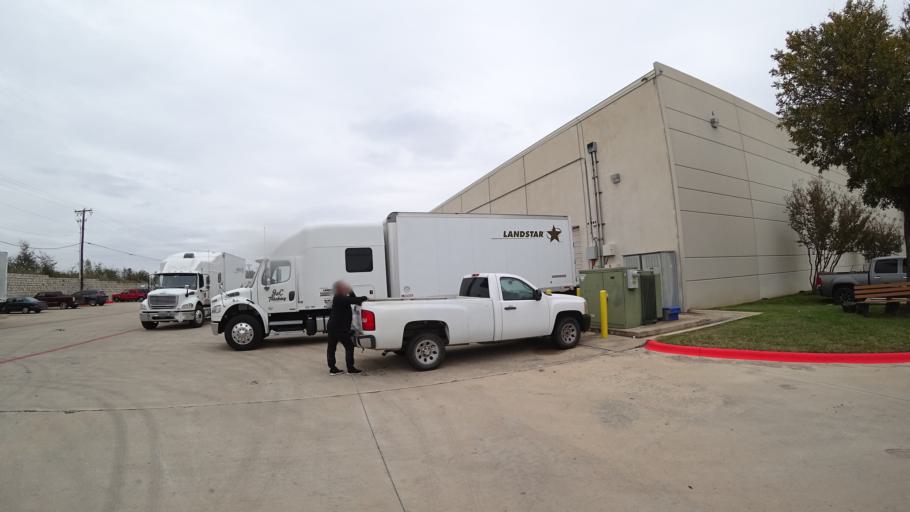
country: US
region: Texas
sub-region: Travis County
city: Wells Branch
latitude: 30.4492
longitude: -97.7065
